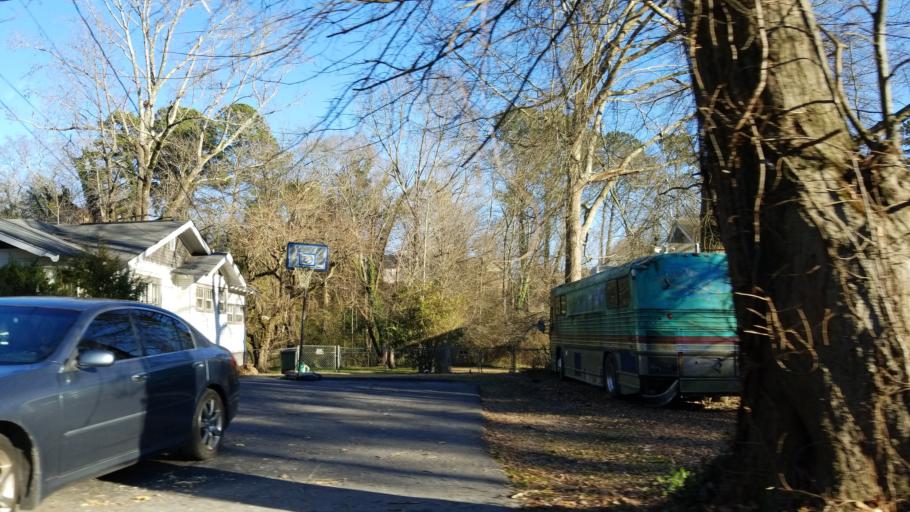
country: US
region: Tennessee
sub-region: Hamilton County
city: East Ridge
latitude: 35.0288
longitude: -85.2470
